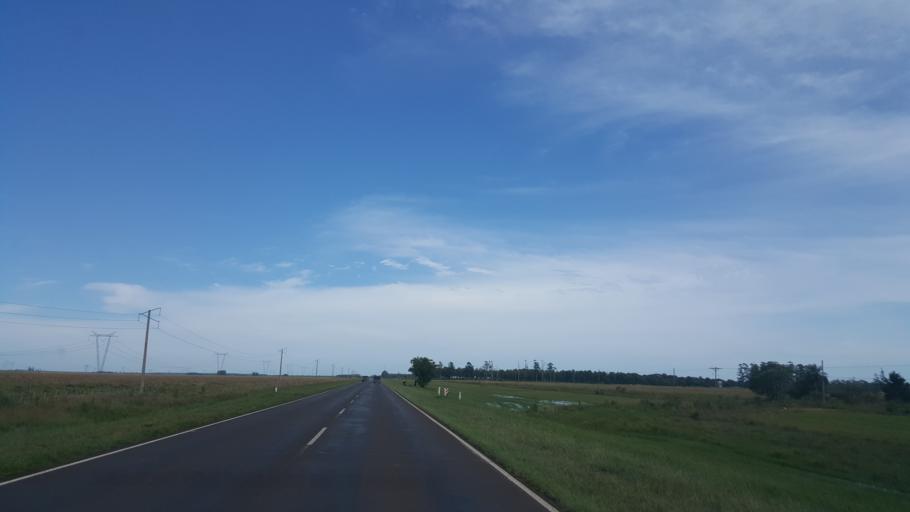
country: AR
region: Corrientes
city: Ituzaingo
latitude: -27.6033
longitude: -56.4509
